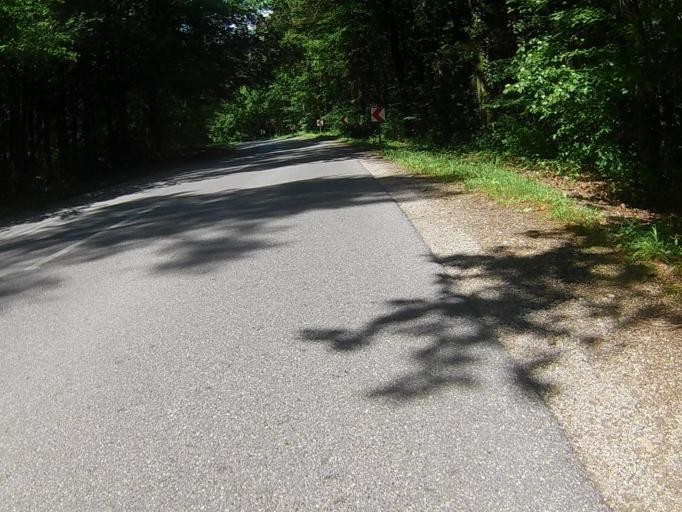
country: SI
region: Miklavz na Dravskem Polju
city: Miklavz na Dravskem Polju
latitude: 46.5025
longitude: 15.6945
